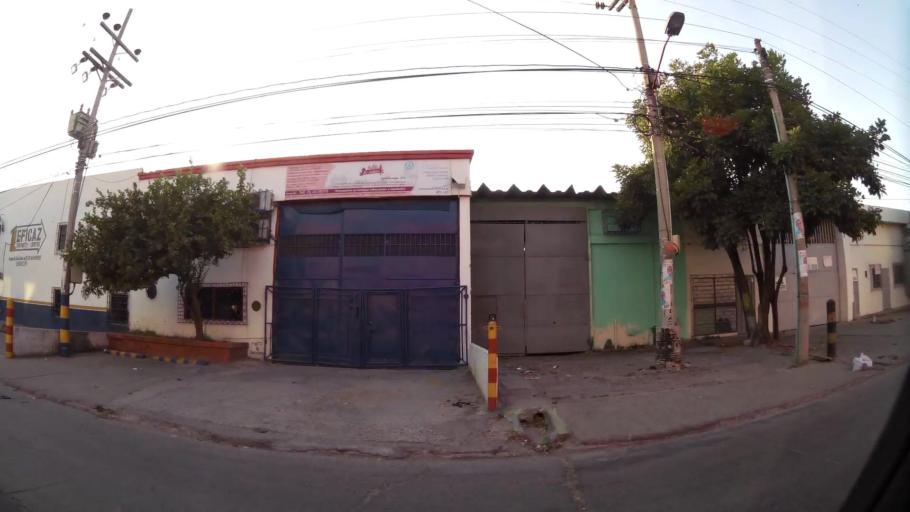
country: CO
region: Bolivar
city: Cartagena
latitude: 10.3930
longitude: -75.5206
